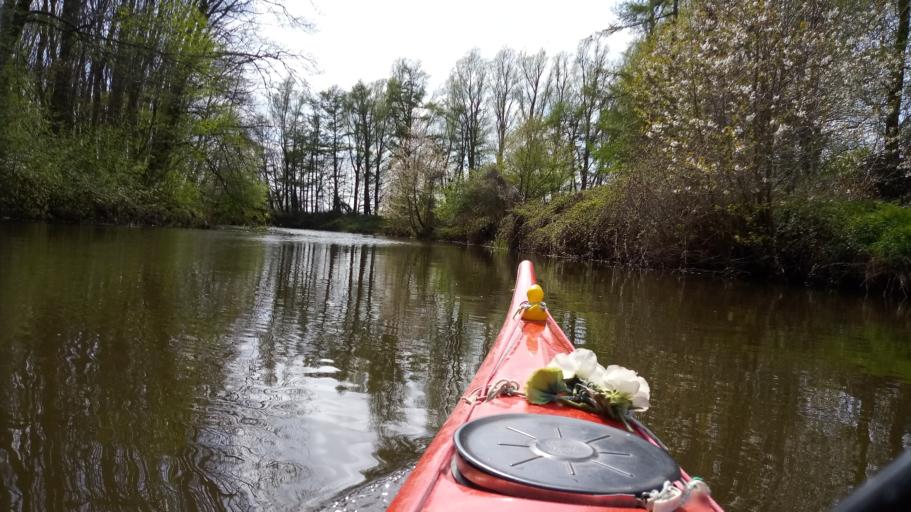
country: NL
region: Overijssel
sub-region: Gemeente Twenterand
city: Den Ham
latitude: 52.4484
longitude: 6.4394
